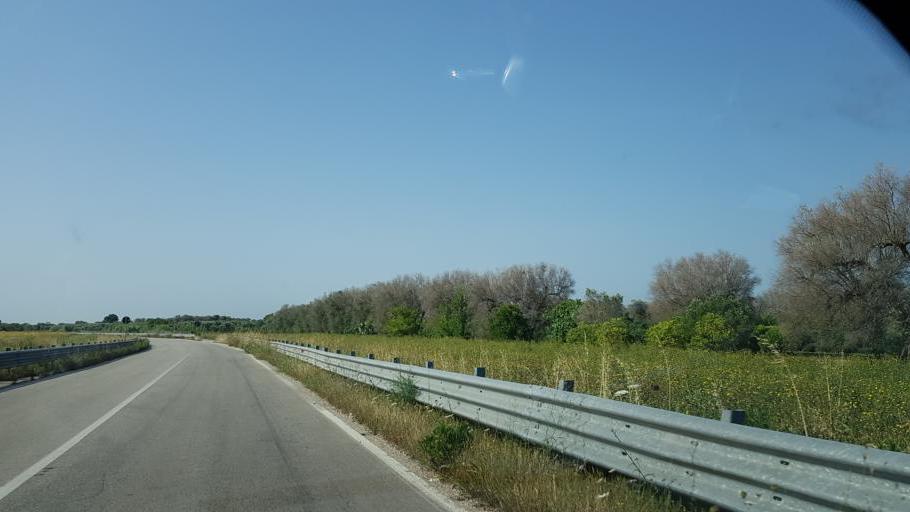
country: IT
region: Apulia
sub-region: Provincia di Brindisi
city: Mesagne
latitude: 40.4980
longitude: 17.8290
